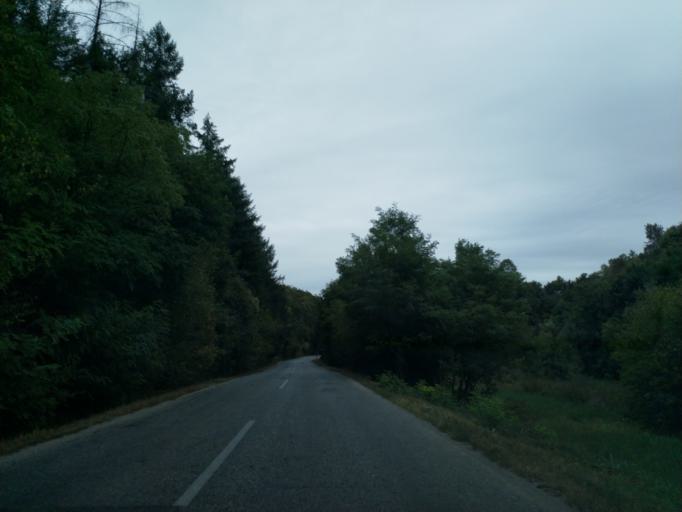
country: RS
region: Central Serbia
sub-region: Pomoravski Okrug
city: Jagodina
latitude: 44.0338
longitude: 21.1920
